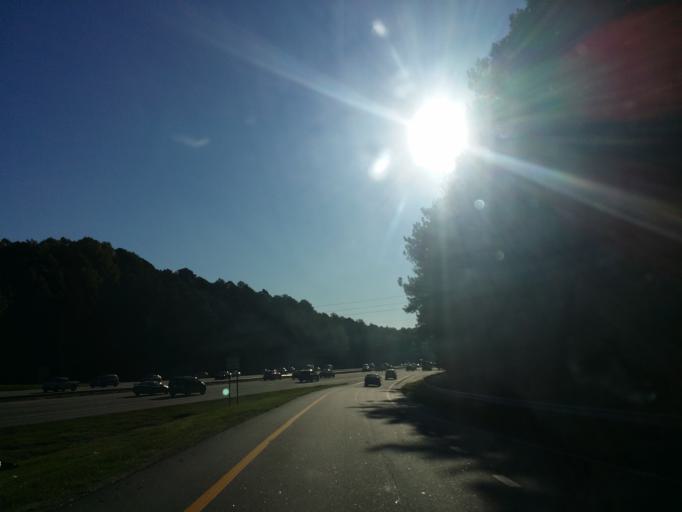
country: US
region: North Carolina
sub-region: Wake County
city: Cary
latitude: 35.8305
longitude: -78.7620
